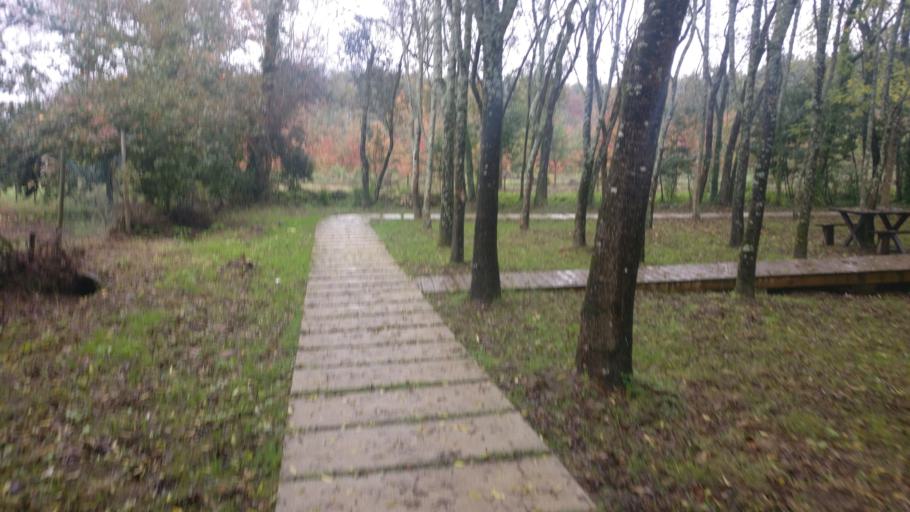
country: PT
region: Viseu
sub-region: Mortagua
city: Mortagua
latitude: 40.3954
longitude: -8.2277
